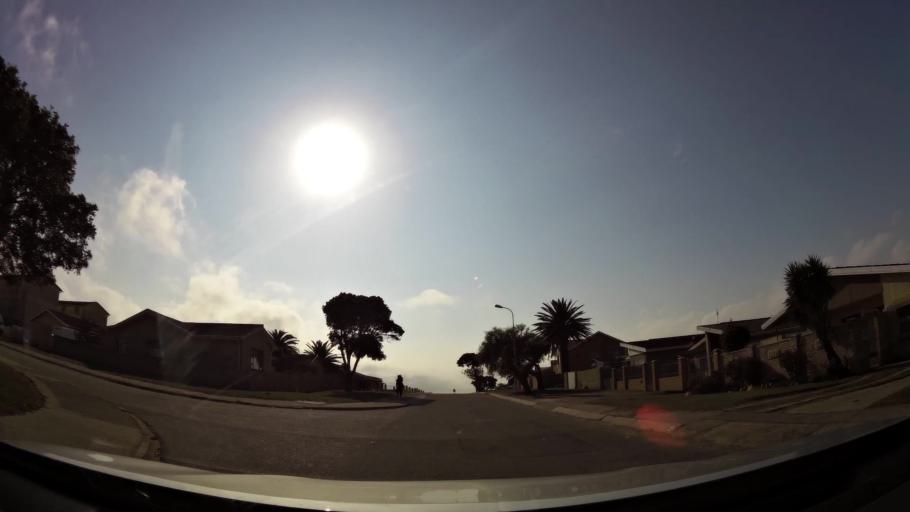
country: ZA
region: Eastern Cape
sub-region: Nelson Mandela Bay Metropolitan Municipality
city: Port Elizabeth
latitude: -33.9237
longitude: 25.5399
